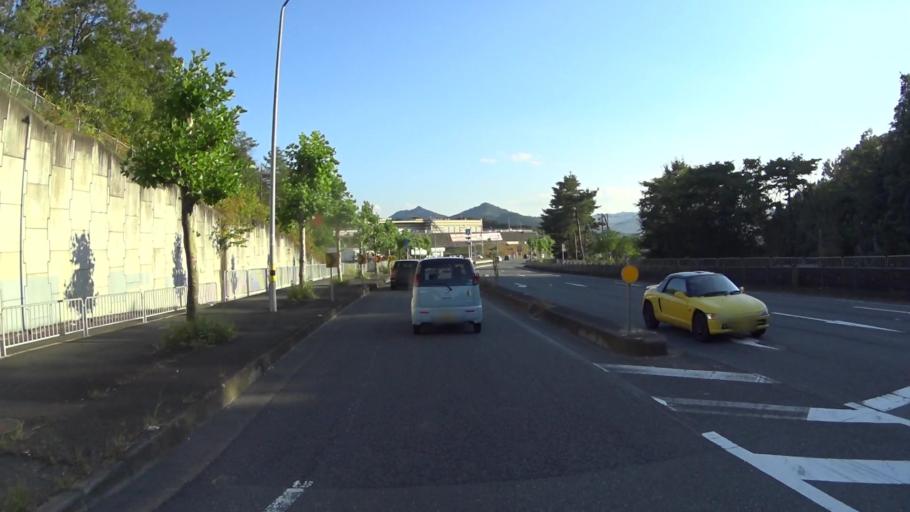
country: JP
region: Kyoto
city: Ayabe
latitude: 35.2777
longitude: 135.1846
